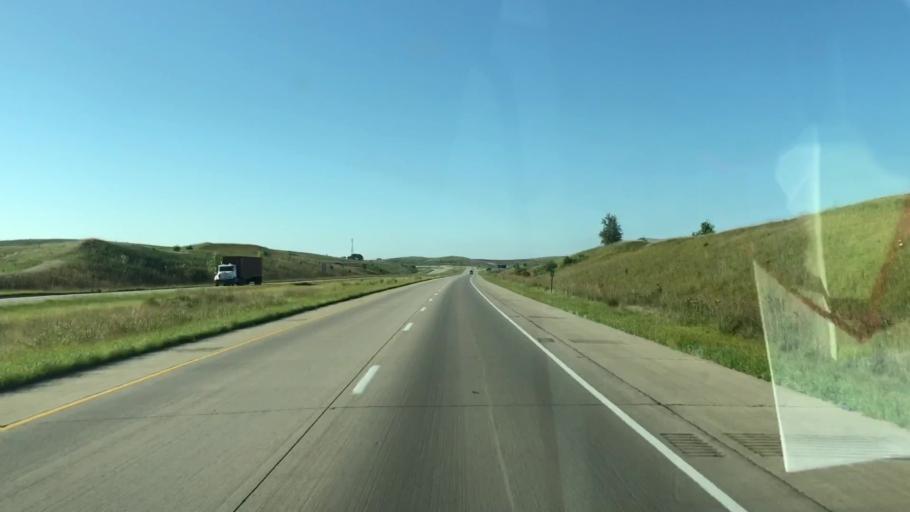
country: US
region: Iowa
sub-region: Woodbury County
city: Sioux City
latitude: 42.5309
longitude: -96.3391
